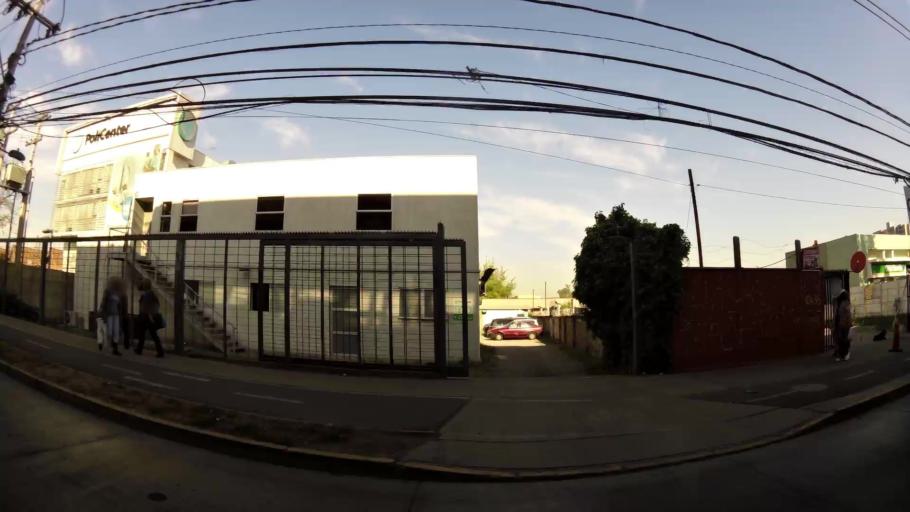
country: CL
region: Santiago Metropolitan
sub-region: Provincia de Santiago
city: La Pintana
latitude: -33.5539
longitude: -70.5867
